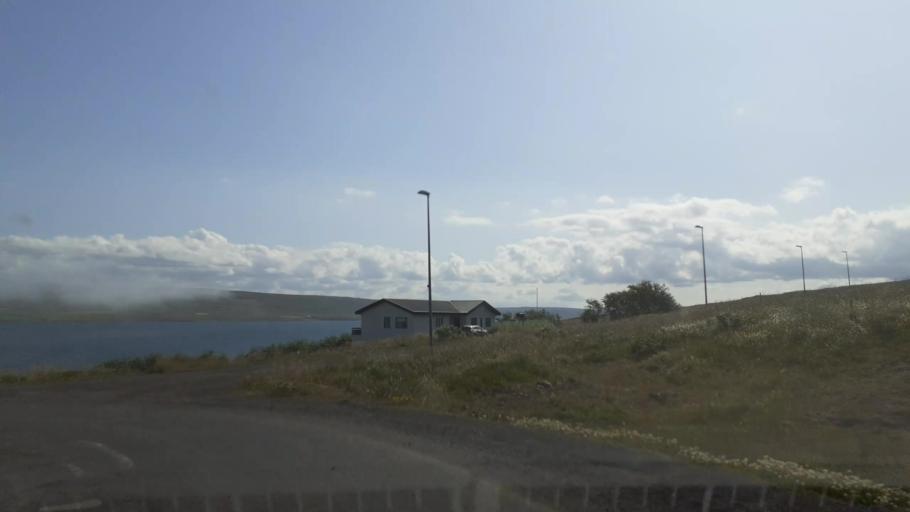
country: IS
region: West
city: Borgarnes
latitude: 65.2063
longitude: -21.0998
